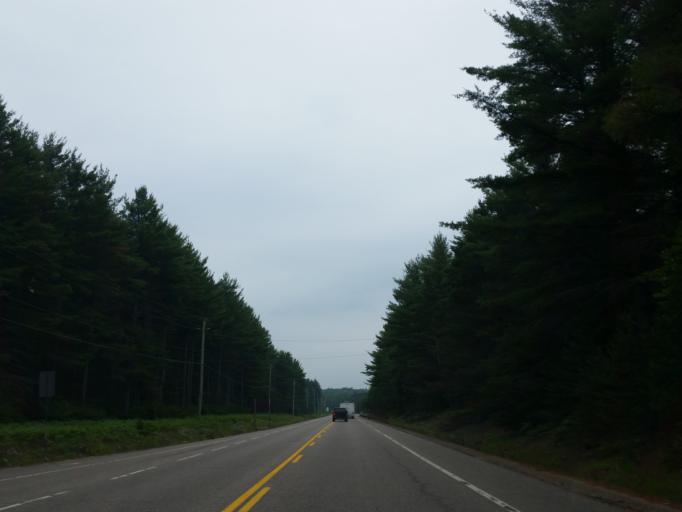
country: CA
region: Ontario
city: Bancroft
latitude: 45.5718
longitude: -78.4436
